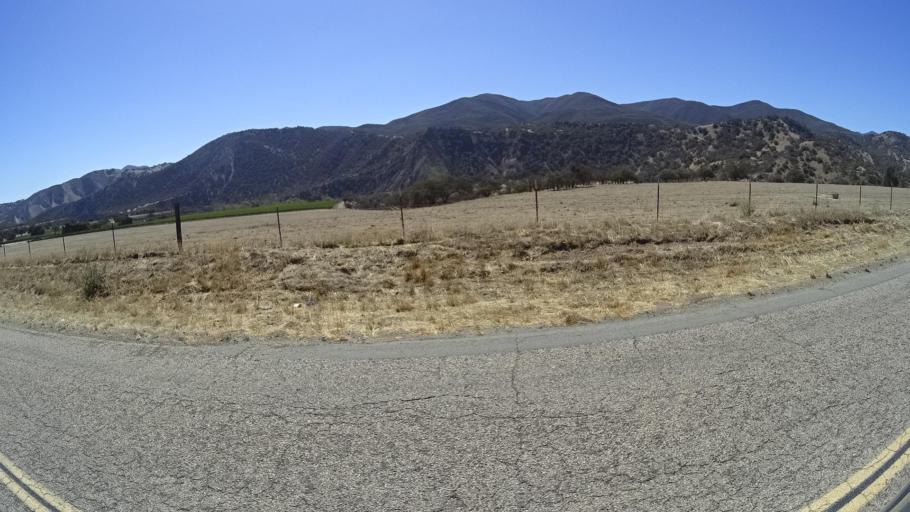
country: US
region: California
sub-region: Monterey County
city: Greenfield
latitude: 36.2683
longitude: -121.3764
